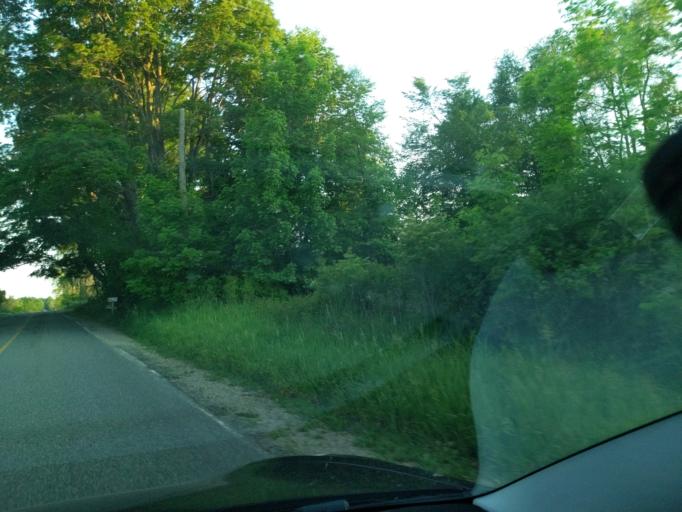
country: US
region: Michigan
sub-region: Barry County
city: Nashville
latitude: 42.5501
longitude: -85.0940
